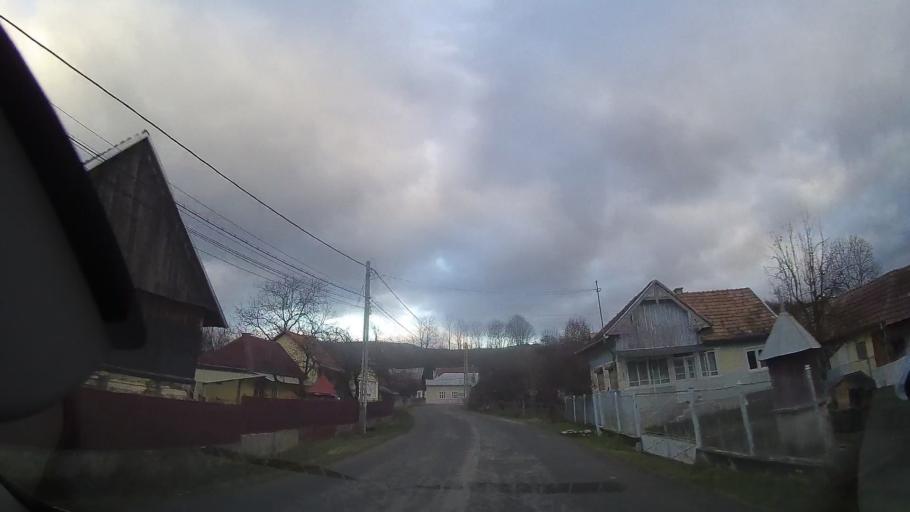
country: RO
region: Cluj
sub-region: Comuna Sancraiu
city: Sancraiu
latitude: 46.8031
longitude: 22.9979
